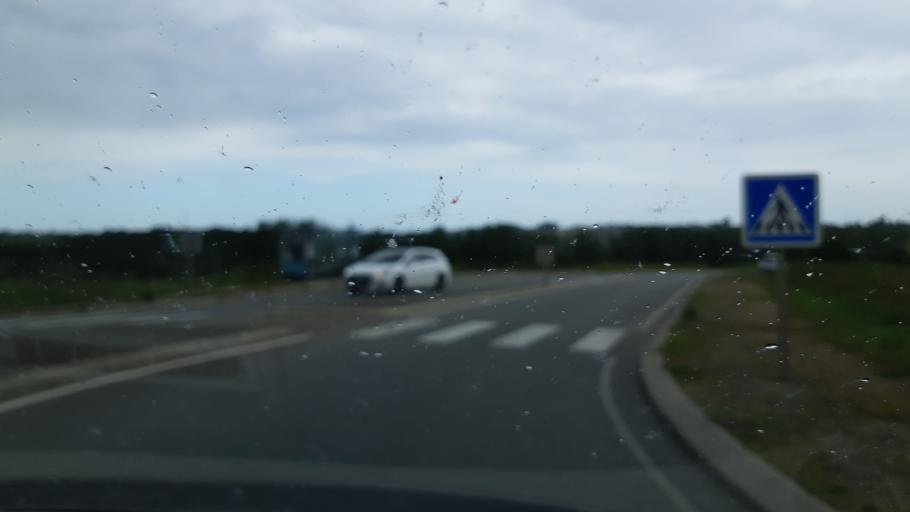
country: FR
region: Brittany
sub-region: Departement du Finistere
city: Plougoulm
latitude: 48.6447
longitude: -4.0485
